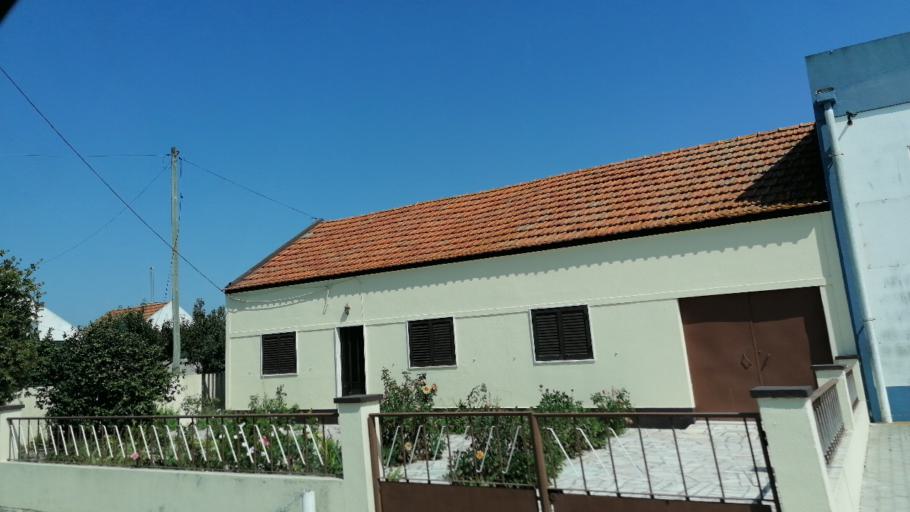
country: PT
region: Santarem
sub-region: Benavente
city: Poceirao
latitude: 38.7099
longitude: -8.7171
